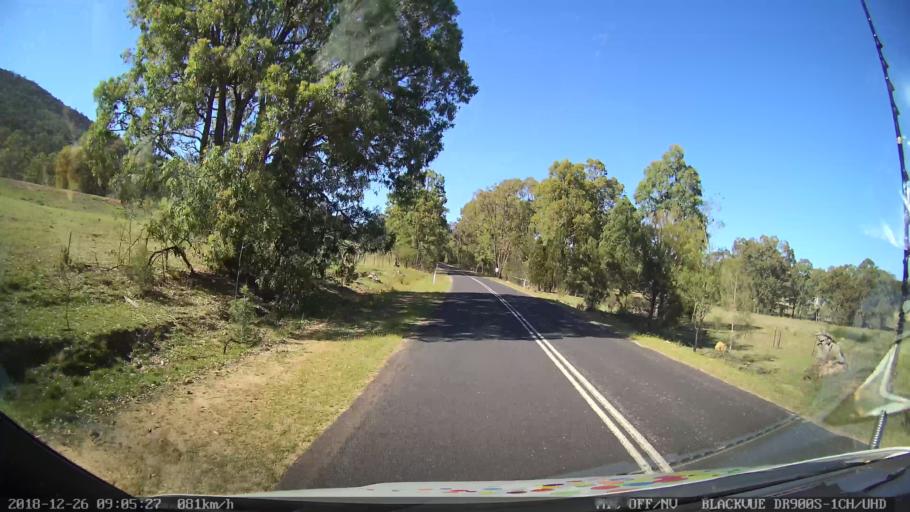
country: AU
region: New South Wales
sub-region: Mid-Western Regional
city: Kandos
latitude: -32.6828
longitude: 150.0075
